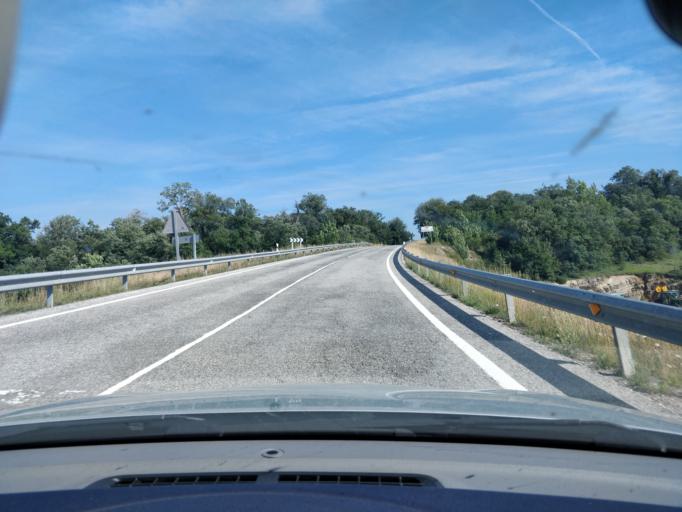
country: ES
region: Cantabria
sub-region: Provincia de Cantabria
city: San Pedro del Romeral
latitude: 42.9657
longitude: -3.7802
